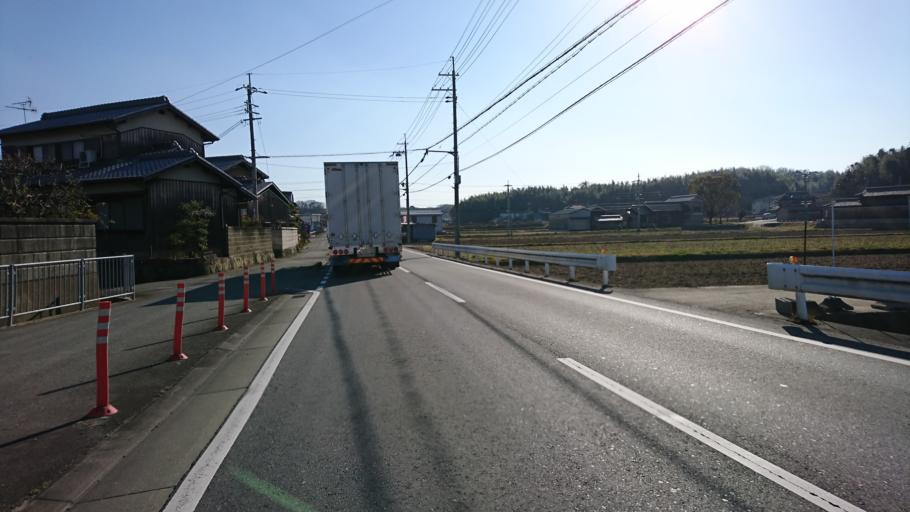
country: JP
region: Hyogo
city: Ono
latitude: 34.7886
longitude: 134.9010
